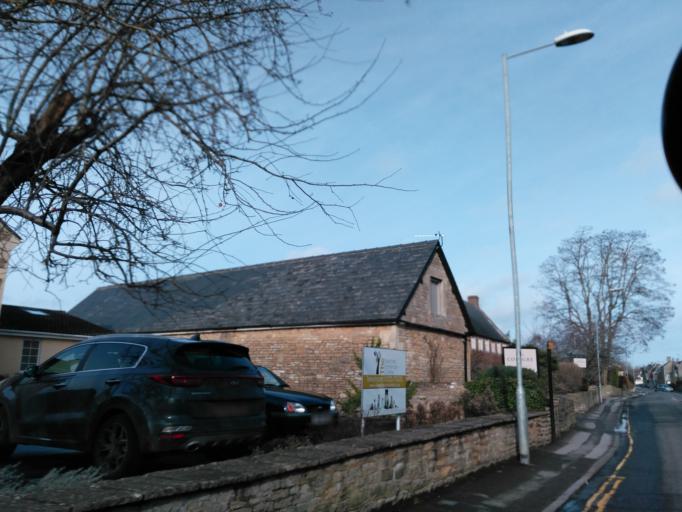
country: GB
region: England
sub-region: Wiltshire
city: Melksham
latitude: 51.3685
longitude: -2.1388
